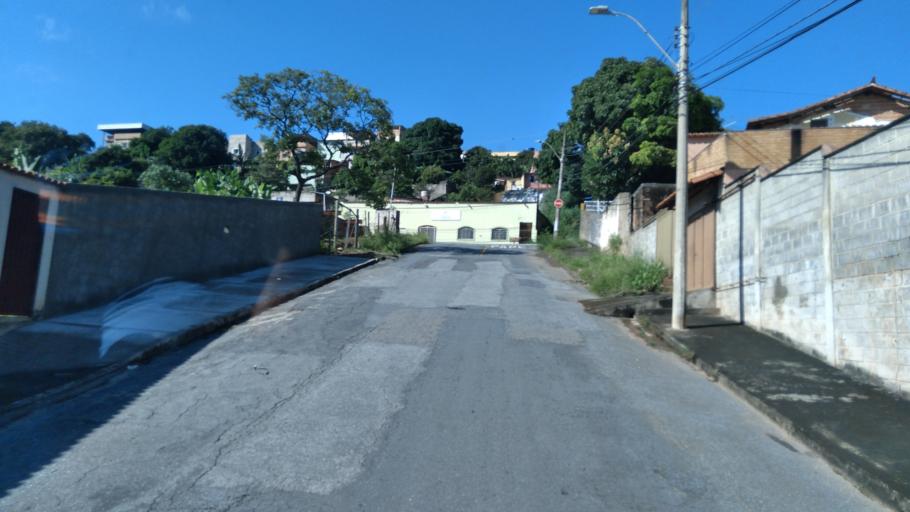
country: BR
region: Minas Gerais
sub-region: Santa Luzia
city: Santa Luzia
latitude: -19.8280
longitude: -43.8994
